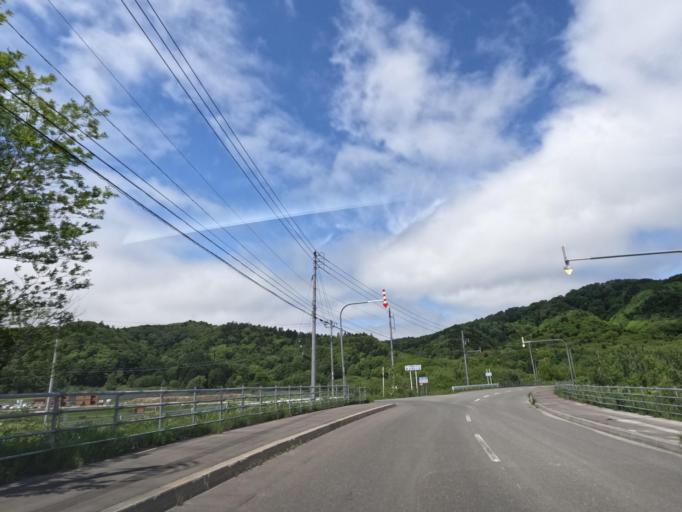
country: JP
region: Hokkaido
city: Tobetsu
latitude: 43.3144
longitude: 141.5566
